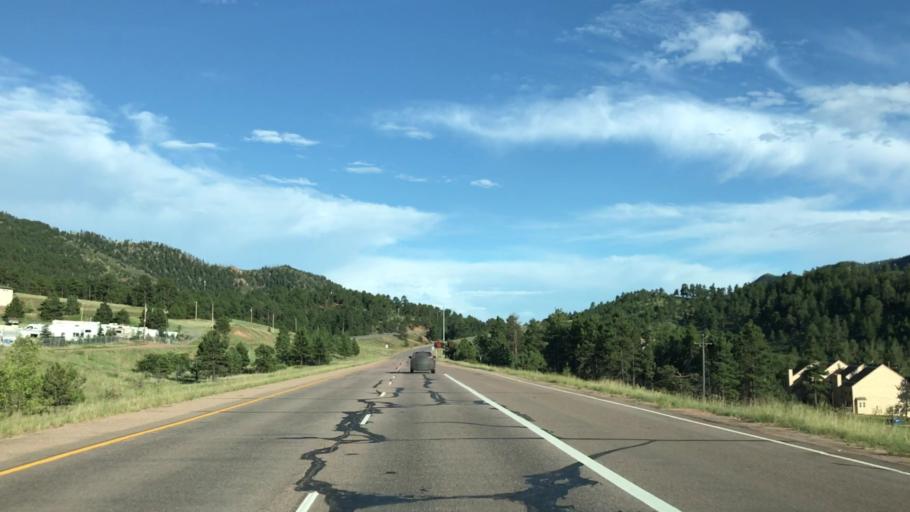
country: US
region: Colorado
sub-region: El Paso County
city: Cascade-Chipita Park
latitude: 38.9416
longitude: -105.0162
